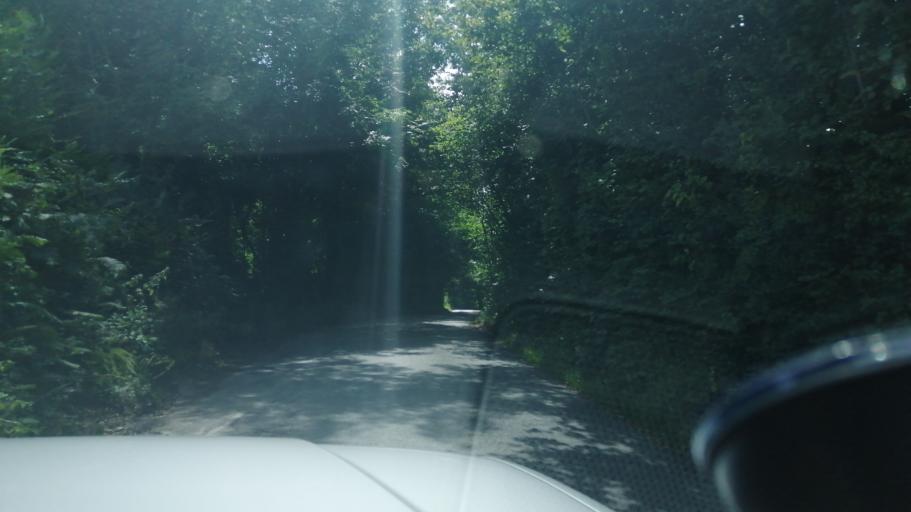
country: GB
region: England
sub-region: Herefordshire
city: Moccas
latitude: 52.0996
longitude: -2.9661
